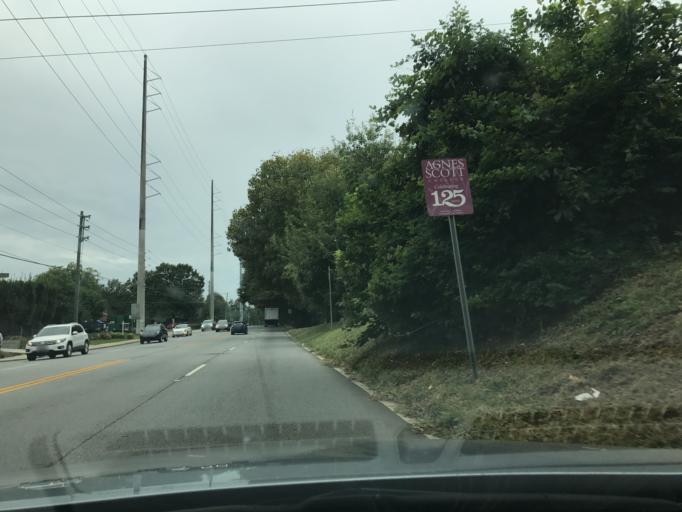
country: US
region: Georgia
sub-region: DeKalb County
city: Decatur
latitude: 33.7725
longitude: -84.2887
